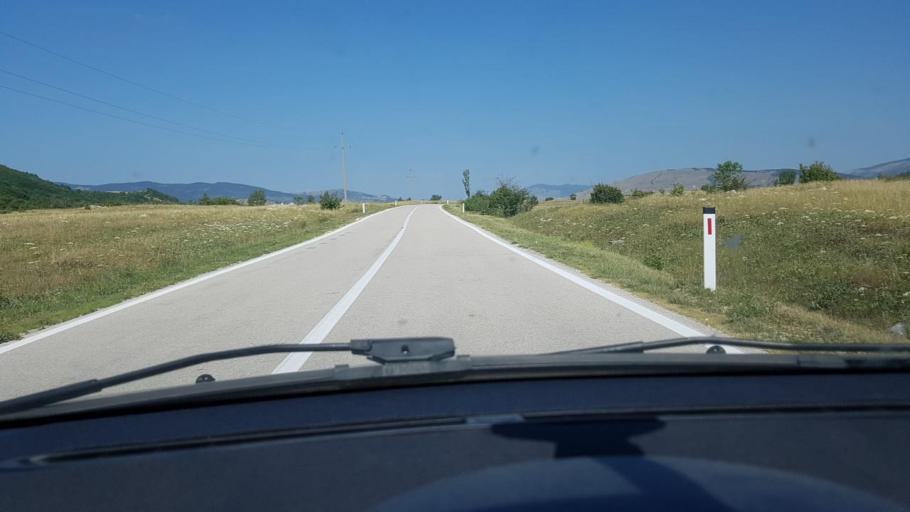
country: BA
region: Federation of Bosnia and Herzegovina
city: Bosansko Grahovo
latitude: 44.1389
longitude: 16.4724
